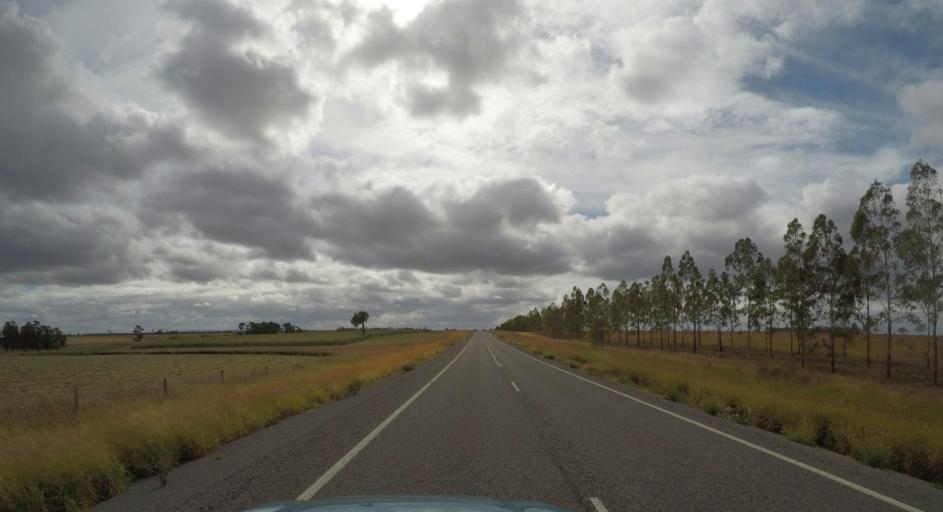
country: AU
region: Queensland
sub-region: South Burnett
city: Wondai
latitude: -26.3261
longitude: 151.2546
